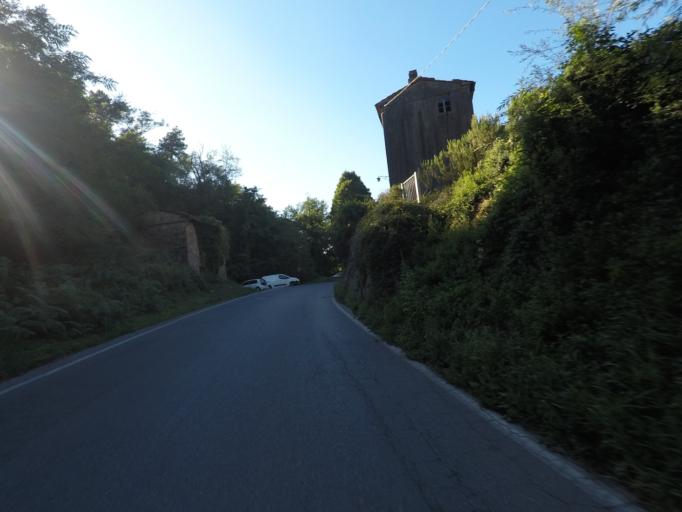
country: IT
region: Tuscany
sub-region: Provincia di Lucca
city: Stiava
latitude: 43.9065
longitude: 10.3496
